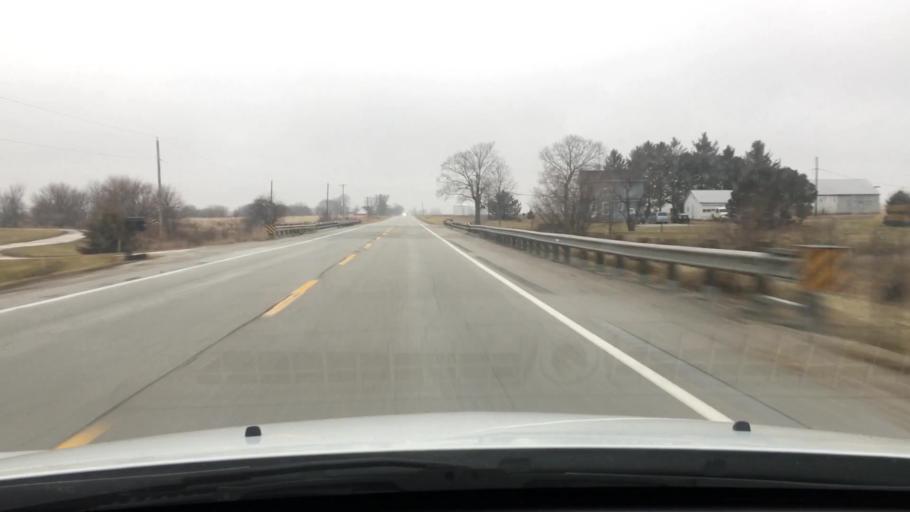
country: US
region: Illinois
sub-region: Livingston County
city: Pontiac
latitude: 40.8726
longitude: -88.7444
